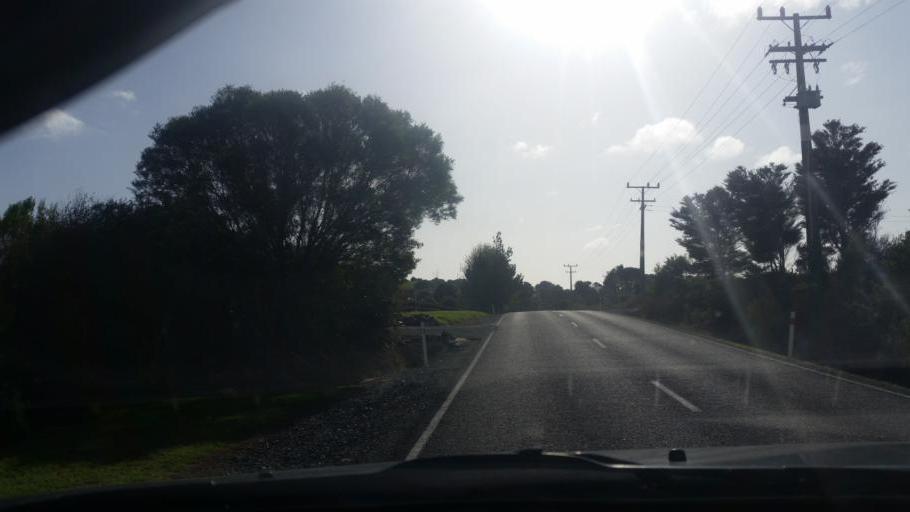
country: NZ
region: Auckland
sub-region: Auckland
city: Wellsford
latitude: -36.0927
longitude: 174.5647
